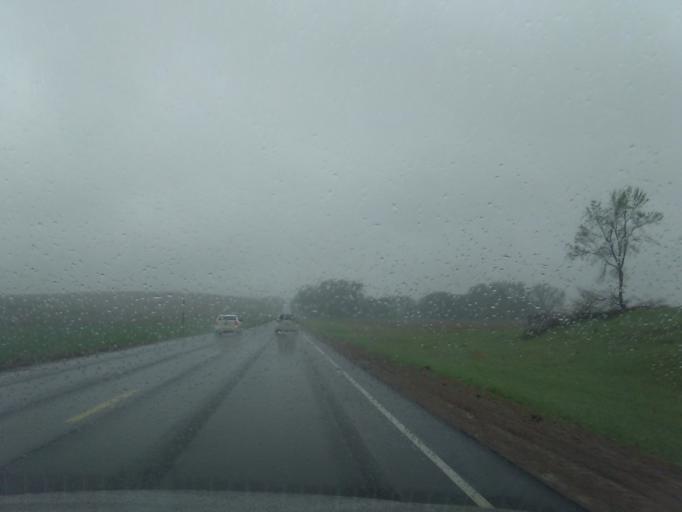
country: US
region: Nebraska
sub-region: Wayne County
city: Wayne
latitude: 42.2249
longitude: -97.1738
